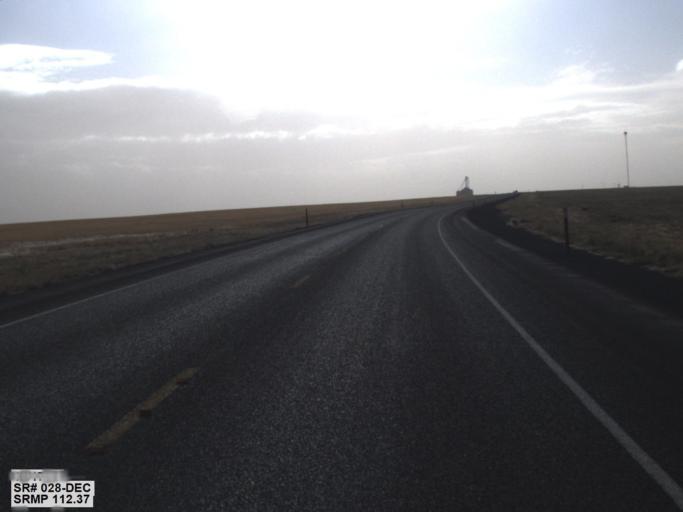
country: US
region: Washington
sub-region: Lincoln County
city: Davenport
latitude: 47.4299
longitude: -118.3413
